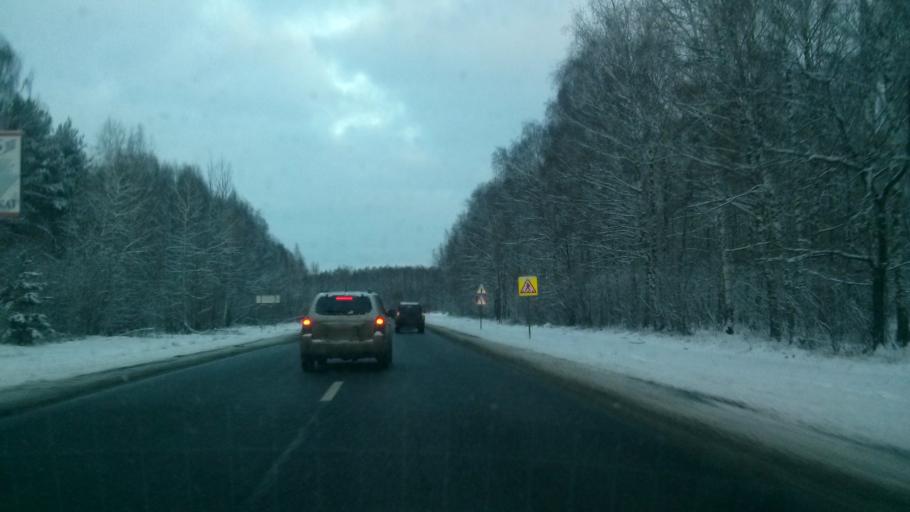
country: RU
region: Nizjnij Novgorod
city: Vorsma
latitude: 56.0111
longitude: 43.3384
